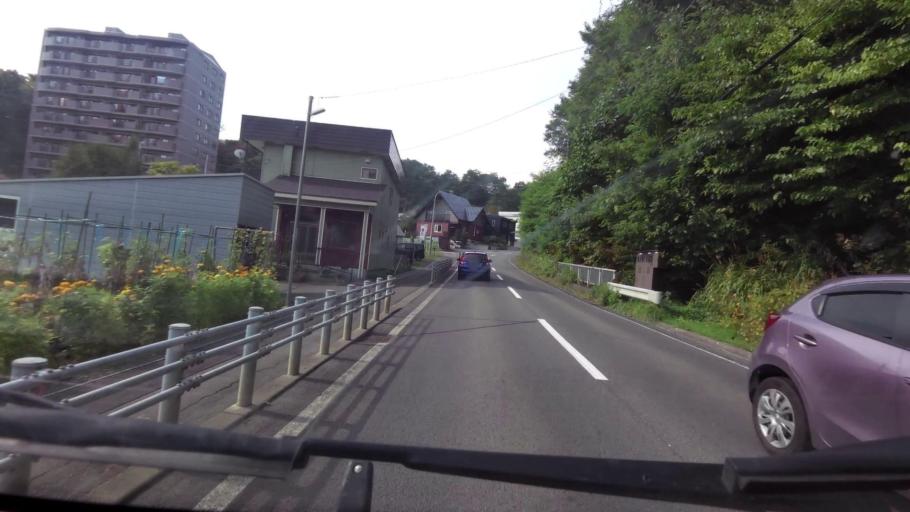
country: JP
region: Hokkaido
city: Otaru
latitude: 43.1421
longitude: 141.1551
